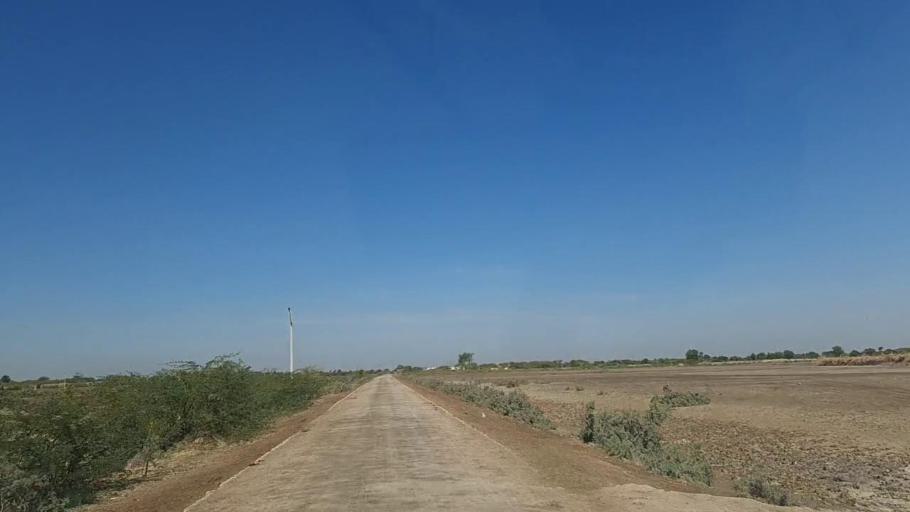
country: PK
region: Sindh
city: Samaro
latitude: 25.3042
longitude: 69.4858
